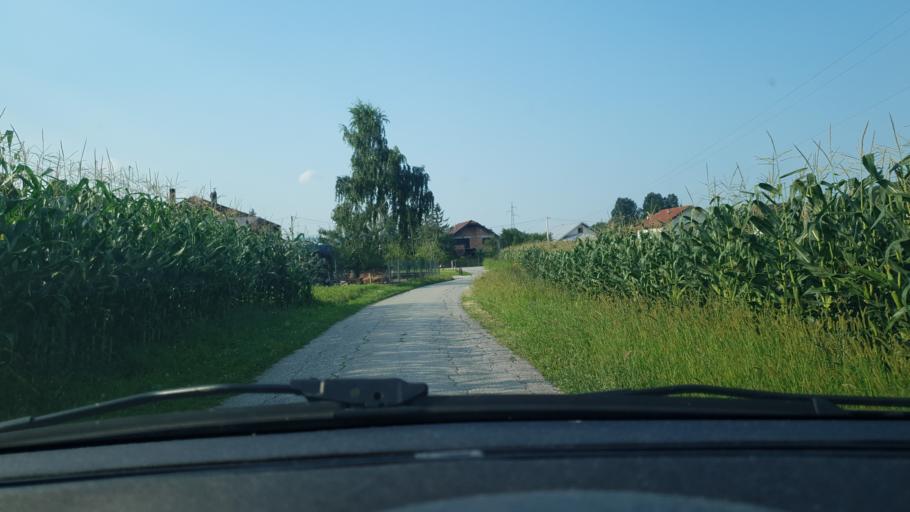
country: HR
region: Krapinsko-Zagorska
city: Zabok
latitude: 46.0601
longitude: 15.9228
